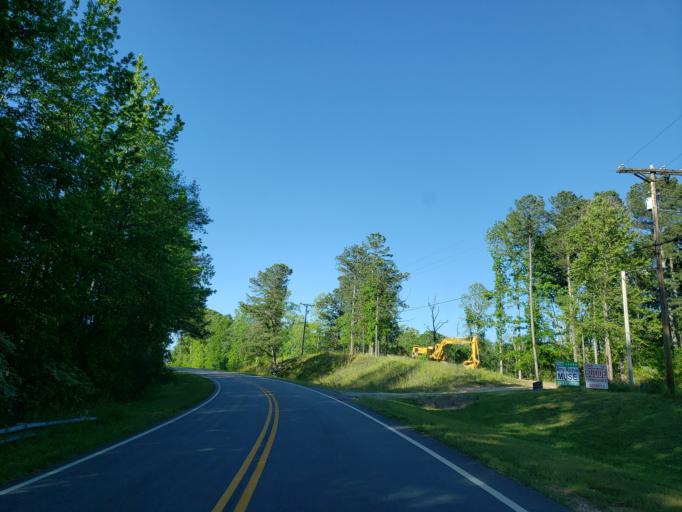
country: US
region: Georgia
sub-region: Haralson County
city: Tallapoosa
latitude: 33.7903
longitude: -85.2880
